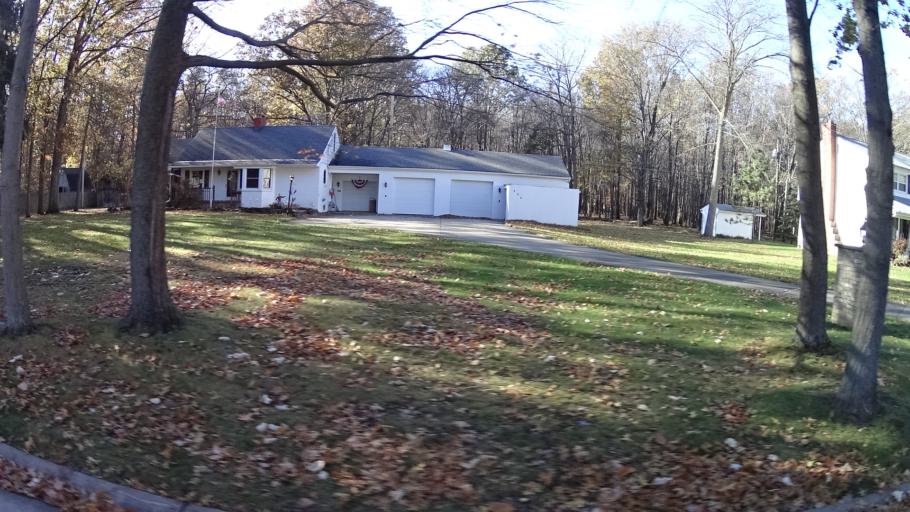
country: US
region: Ohio
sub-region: Lorain County
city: Avon Lake
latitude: 41.5071
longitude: -82.0046
